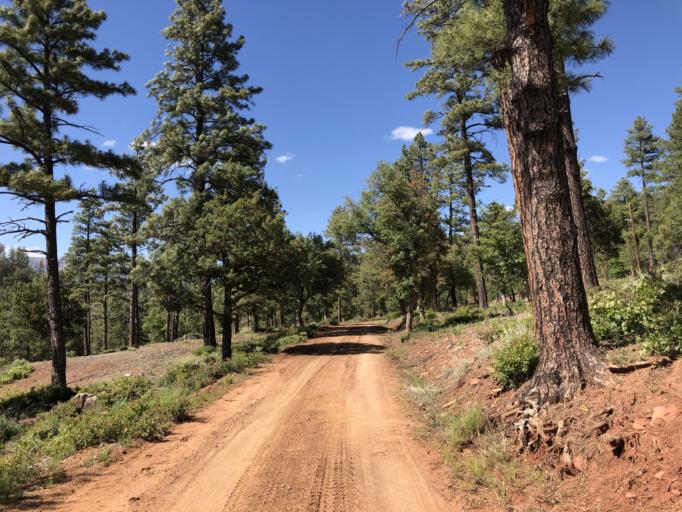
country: US
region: Arizona
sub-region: Gila County
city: Star Valley
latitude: 34.3574
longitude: -111.2812
